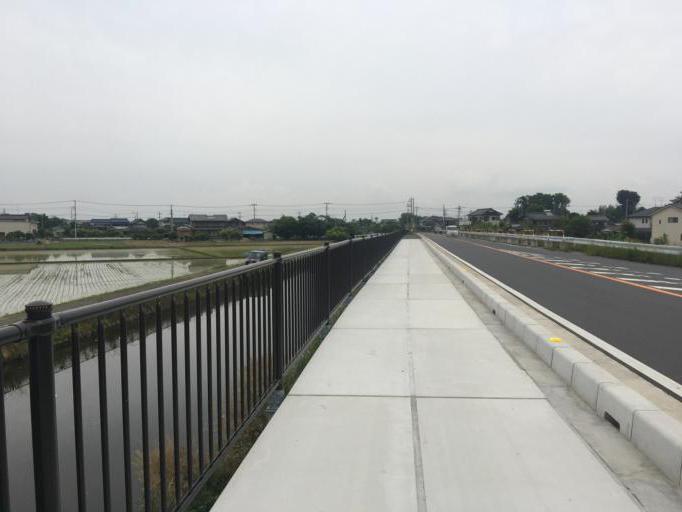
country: JP
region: Saitama
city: Fukiage-fujimi
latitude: 36.0217
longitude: 139.4408
